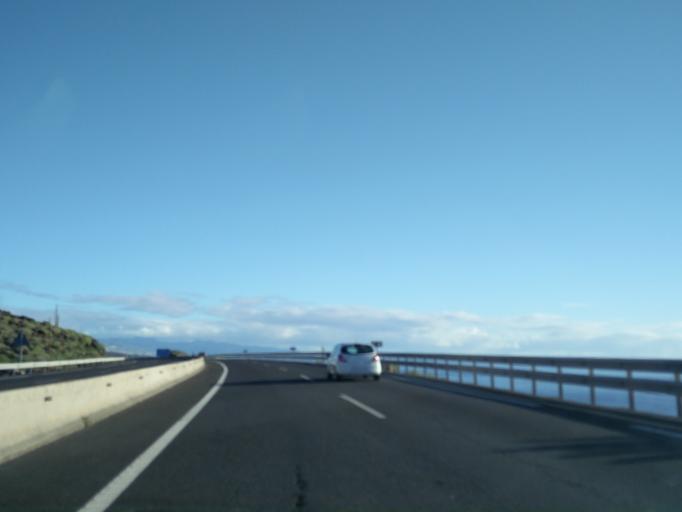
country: ES
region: Canary Islands
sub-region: Provincia de Santa Cruz de Tenerife
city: Fasnia
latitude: 28.2630
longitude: -16.3905
